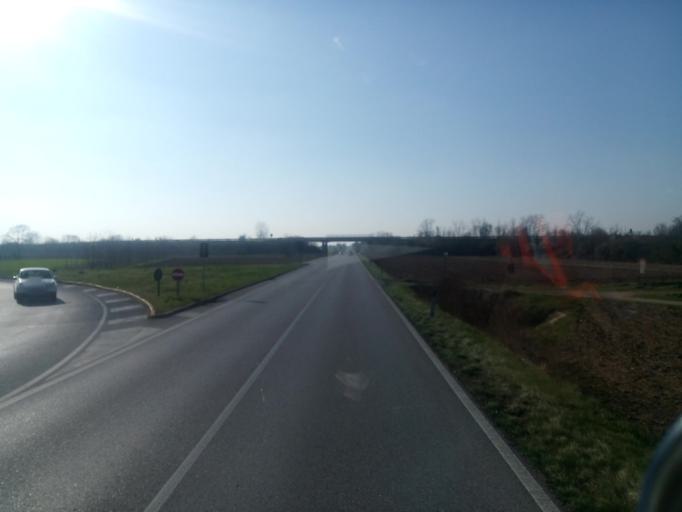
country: IT
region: Friuli Venezia Giulia
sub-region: Provincia di Udine
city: Bertiolo
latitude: 45.9447
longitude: 13.0882
